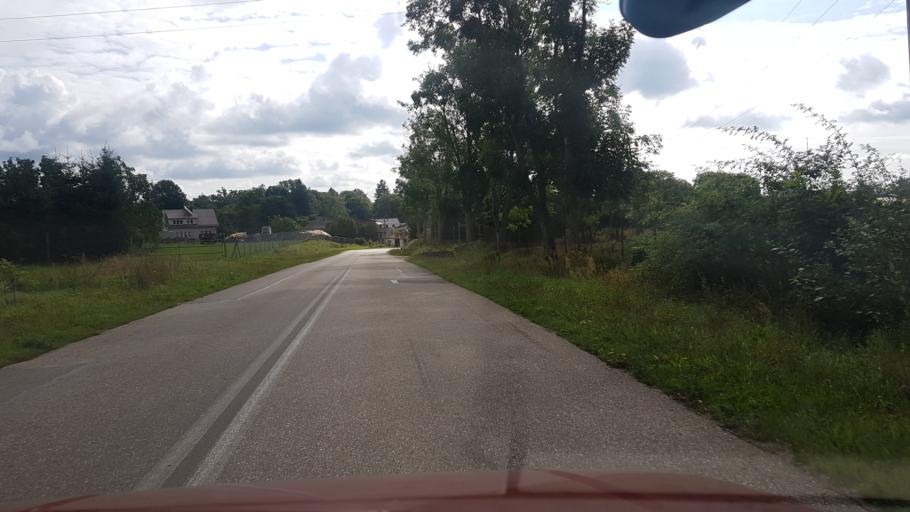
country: PL
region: Pomeranian Voivodeship
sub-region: Powiat bytowski
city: Miastko
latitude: 54.0865
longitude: 16.8514
